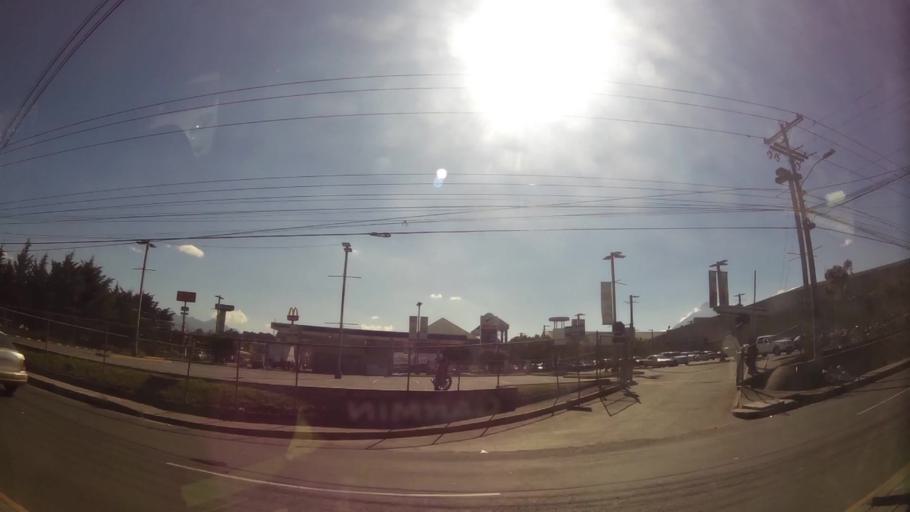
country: GT
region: Guatemala
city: Villa Nueva
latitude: 14.5320
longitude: -90.5967
